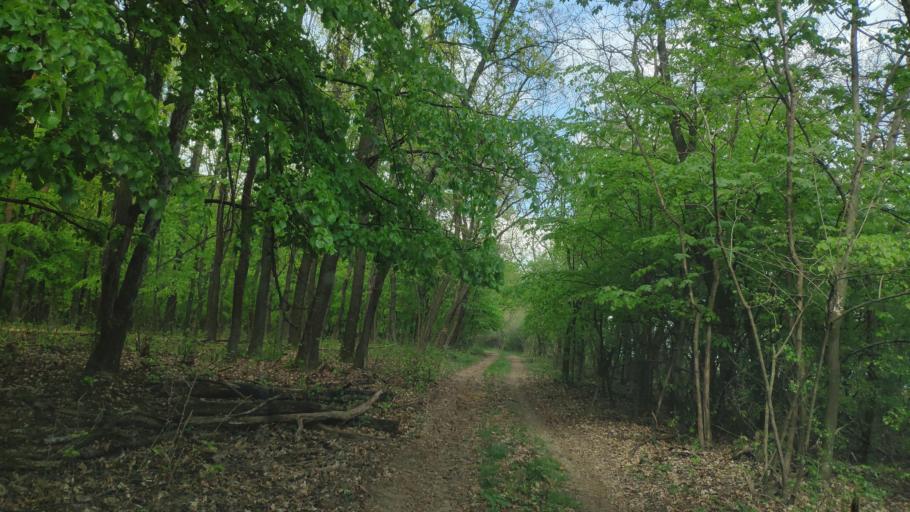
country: SK
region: Kosicky
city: Moldava nad Bodvou
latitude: 48.5434
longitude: 20.9445
